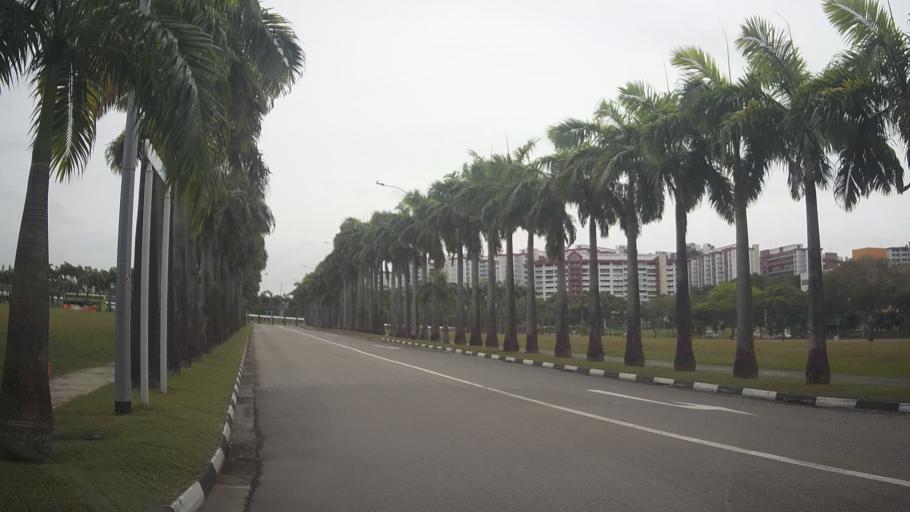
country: MY
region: Johor
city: Johor Bahru
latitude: 1.4407
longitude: 103.7841
